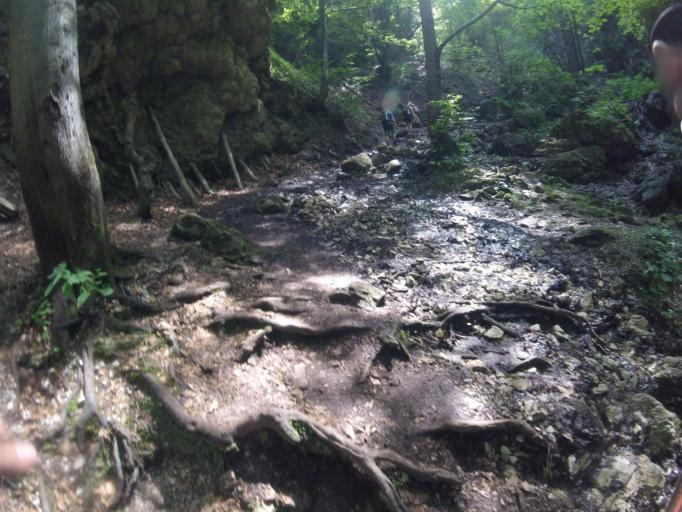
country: SK
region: Zilinsky
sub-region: Okres Zilina
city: Terchova
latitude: 49.2422
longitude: 19.0922
